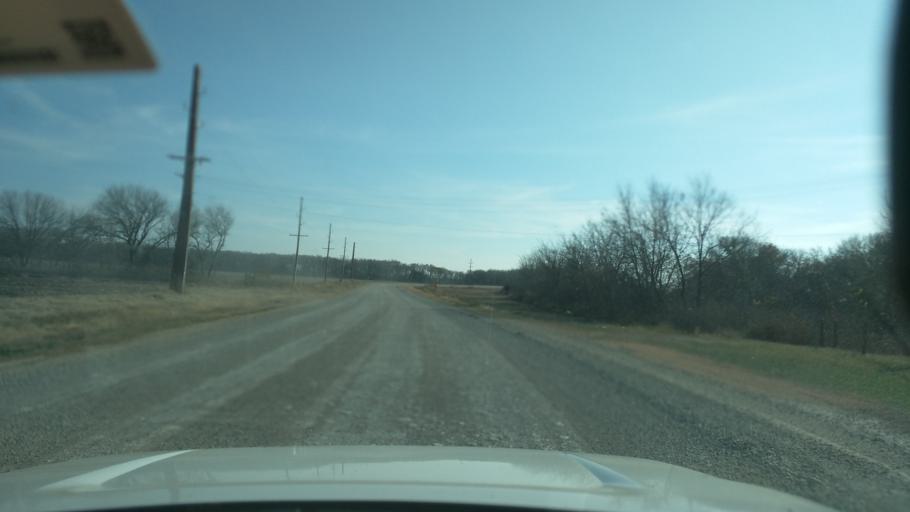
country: US
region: Kansas
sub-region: Lyon County
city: Emporia
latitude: 38.3869
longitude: -96.2078
